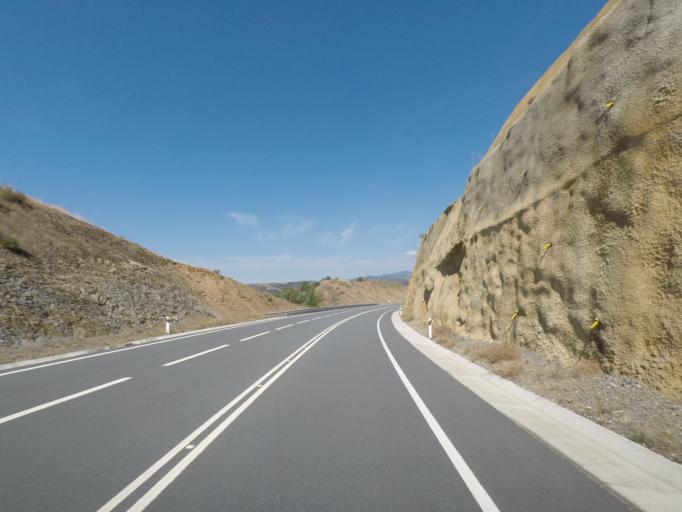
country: PT
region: Braganca
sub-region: Alfandega da Fe
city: Alfandega da Fe
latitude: 41.2970
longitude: -6.8989
